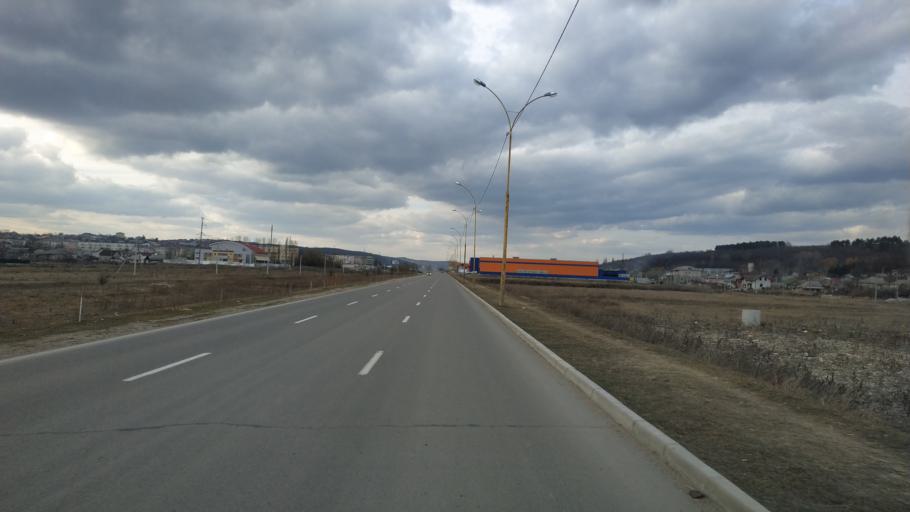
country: MD
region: Hincesti
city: Hincesti
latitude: 46.8267
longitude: 28.6034
